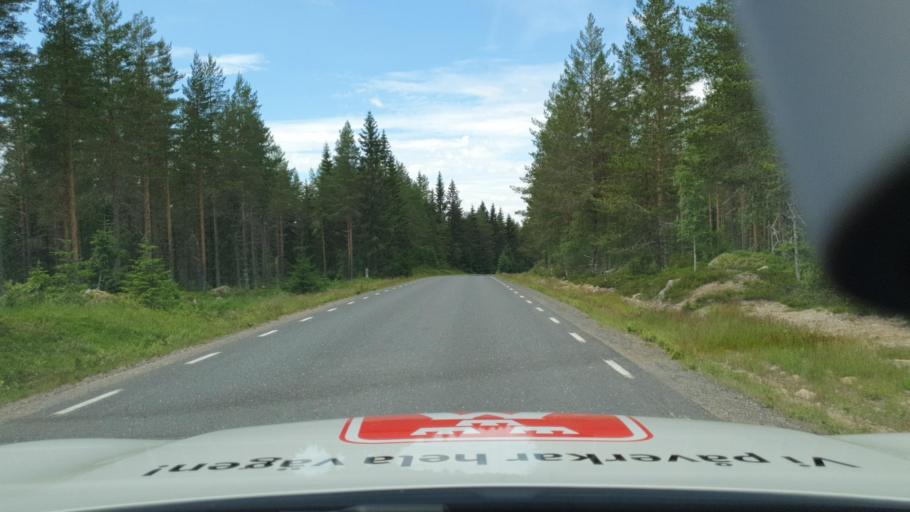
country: SE
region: Vaermland
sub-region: Torsby Kommun
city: Torsby
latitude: 60.5367
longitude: 12.8080
